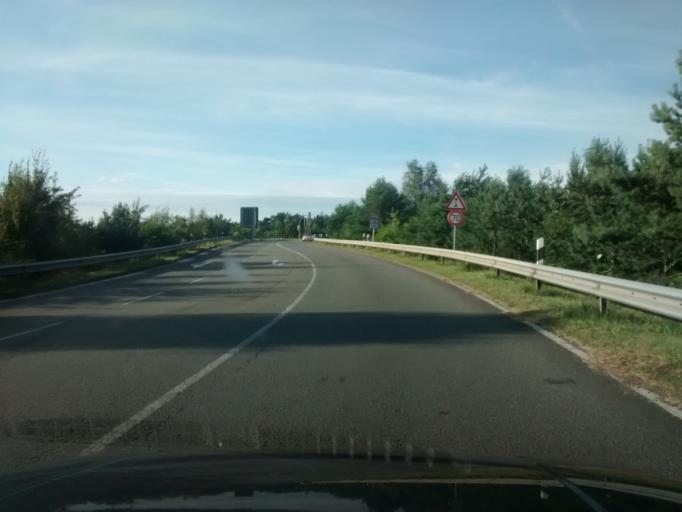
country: DE
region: Lower Saxony
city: Meppen
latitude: 52.7120
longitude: 7.2962
